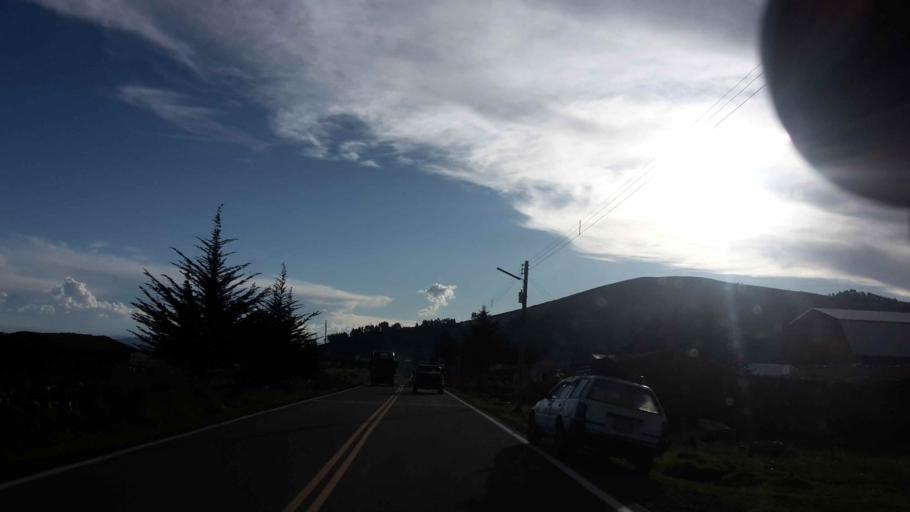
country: BO
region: Cochabamba
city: Arani
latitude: -17.5498
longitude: -65.6847
